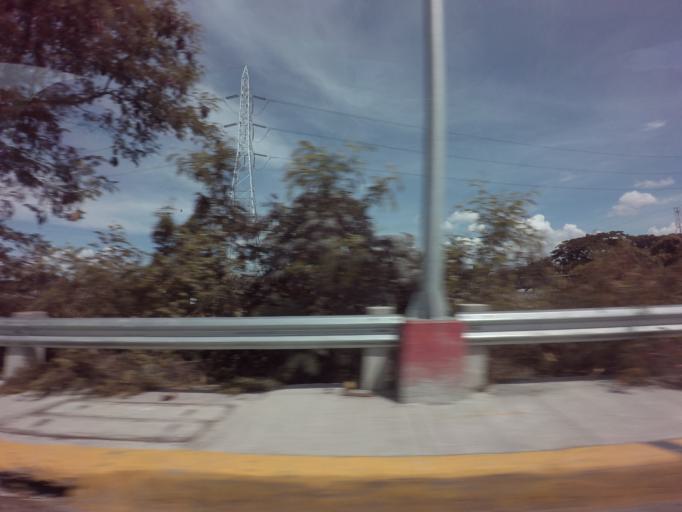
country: PH
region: Calabarzon
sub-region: Province of Rizal
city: Taguig
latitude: 14.5096
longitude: 121.0705
